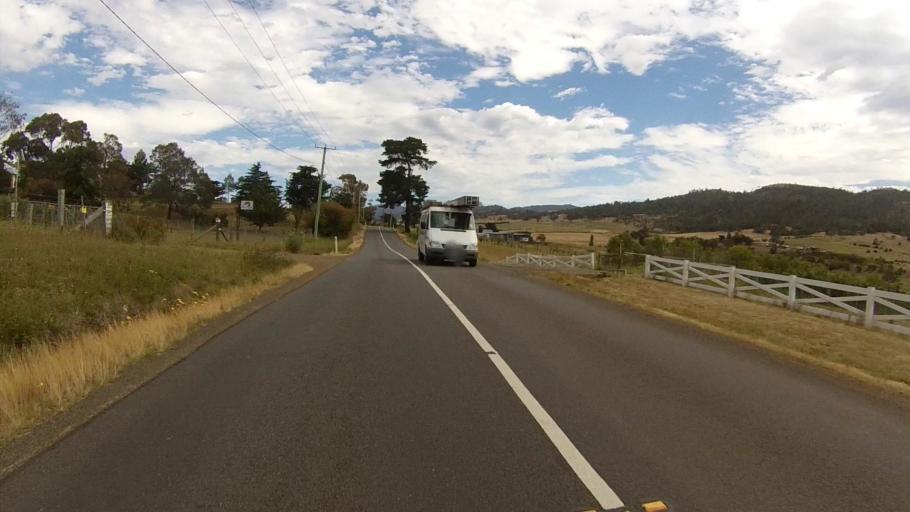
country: AU
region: Tasmania
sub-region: Brighton
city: Old Beach
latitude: -42.7082
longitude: 147.3696
